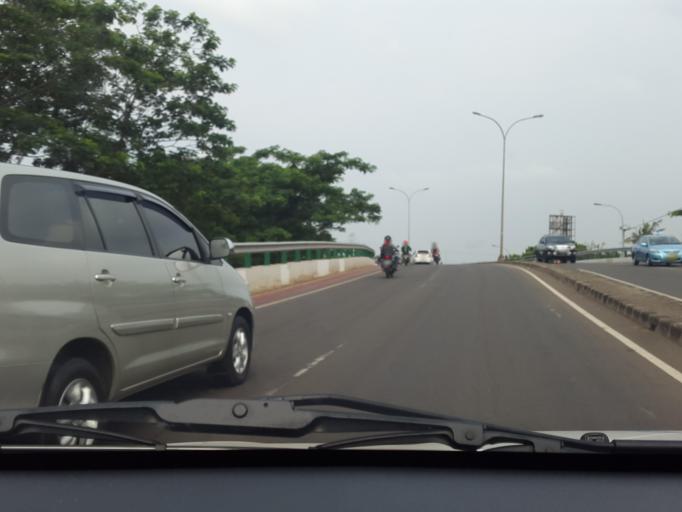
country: ID
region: Banten
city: South Tangerang
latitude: -6.2750
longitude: 106.7050
